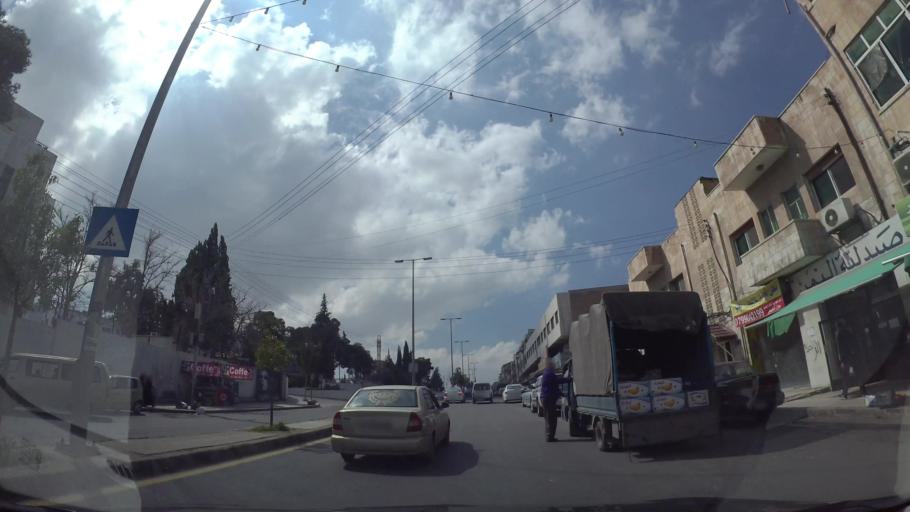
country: JO
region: Amman
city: Amman
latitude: 31.9822
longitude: 35.9905
